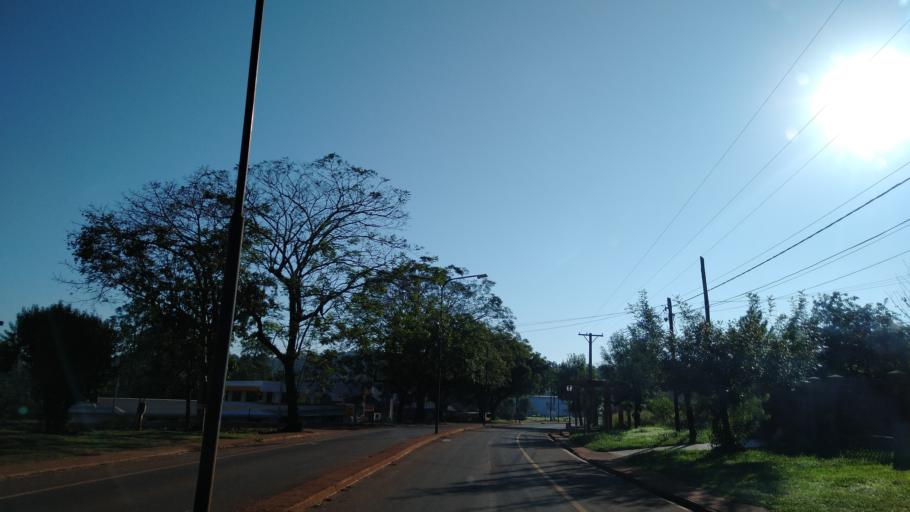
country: AR
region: Misiones
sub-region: Departamento de Montecarlo
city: Montecarlo
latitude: -26.5725
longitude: -54.7429
